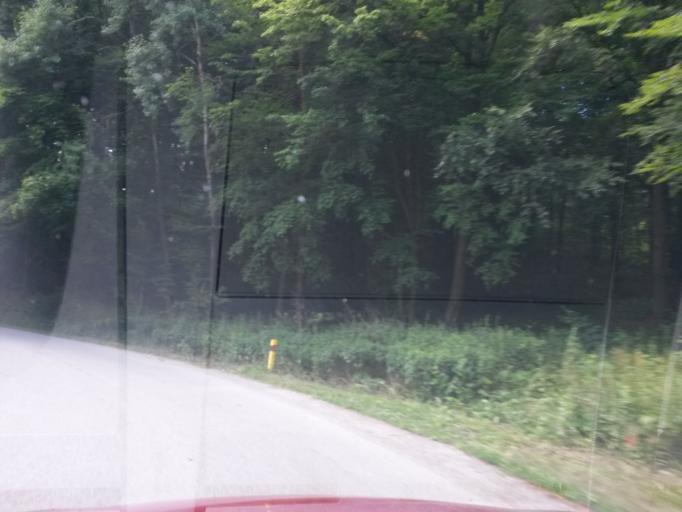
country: SK
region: Kosicky
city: Gelnica
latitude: 48.9506
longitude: 21.0612
